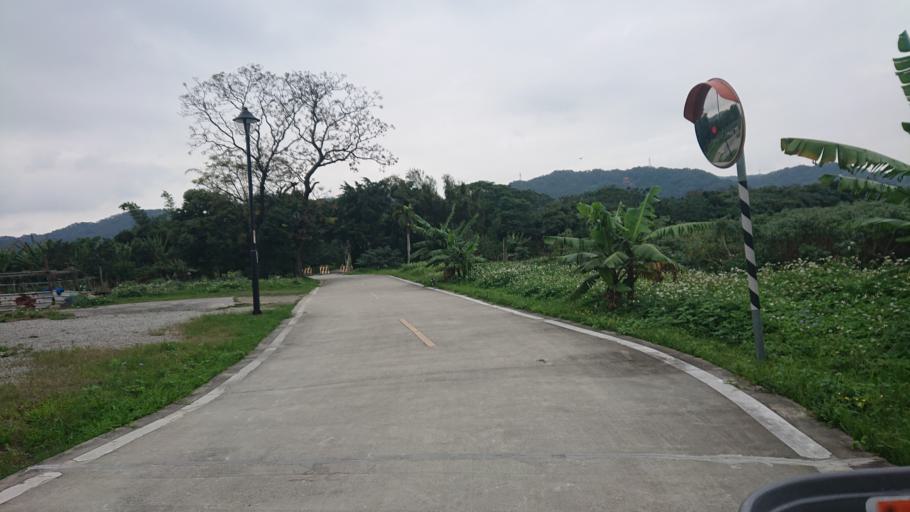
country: TW
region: Taiwan
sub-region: Taoyuan
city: Taoyuan
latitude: 24.9500
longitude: 121.3644
